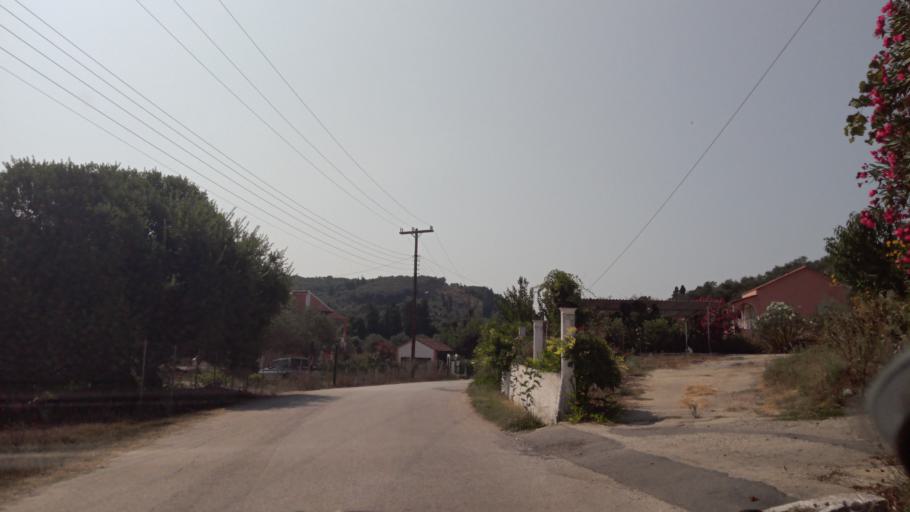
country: GR
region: Ionian Islands
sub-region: Nomos Kerkyras
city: Perivoli
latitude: 39.4036
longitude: 20.0268
